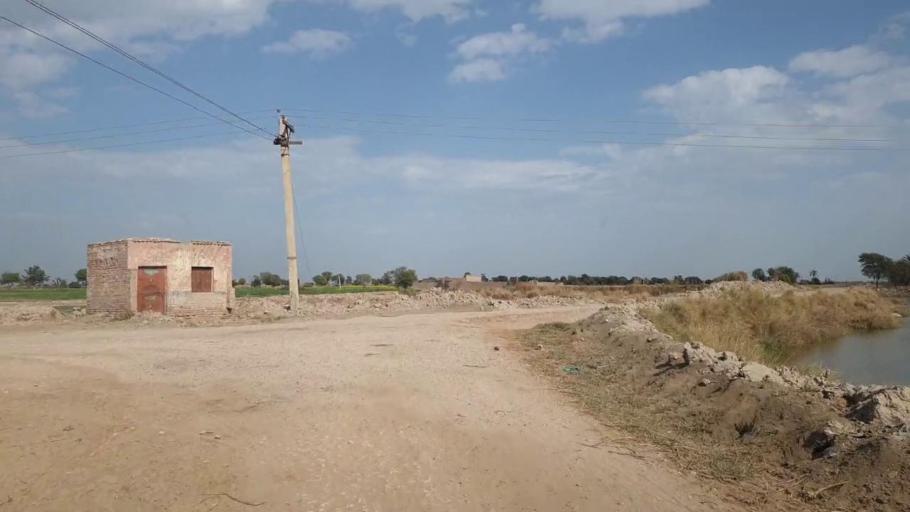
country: PK
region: Sindh
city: Shahdadpur
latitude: 26.0063
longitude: 68.4582
